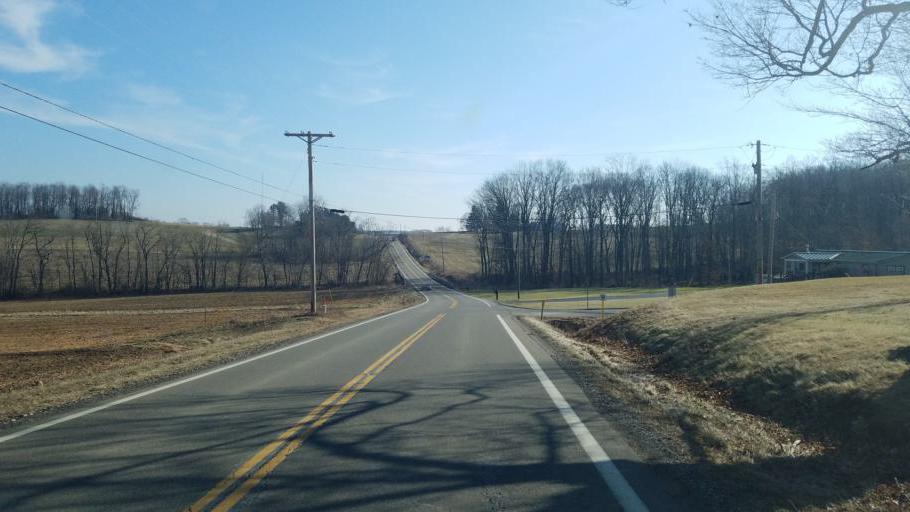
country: US
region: Ohio
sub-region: Wayne County
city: Shreve
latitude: 40.5770
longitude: -82.0315
